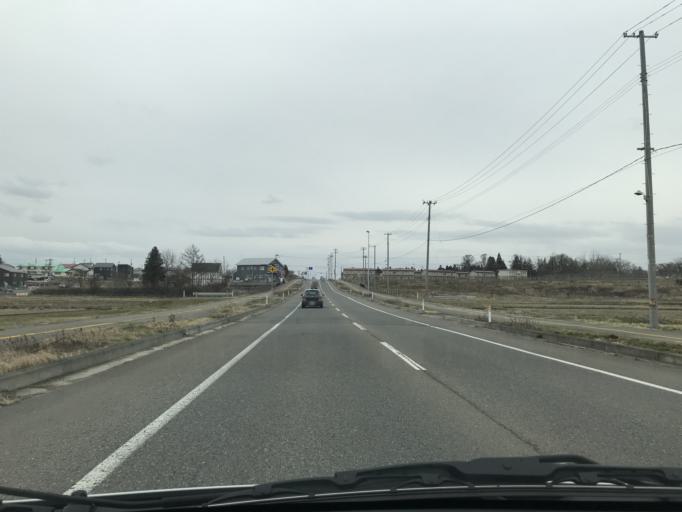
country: JP
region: Iwate
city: Hanamaki
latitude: 39.3734
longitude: 141.1120
